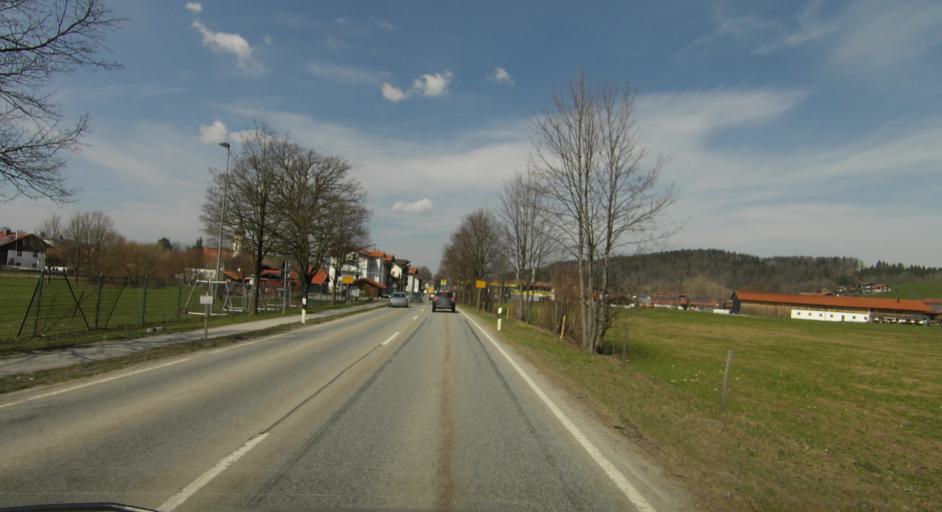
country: DE
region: Bavaria
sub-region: Upper Bavaria
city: Hausham
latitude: 47.7452
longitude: 11.8455
